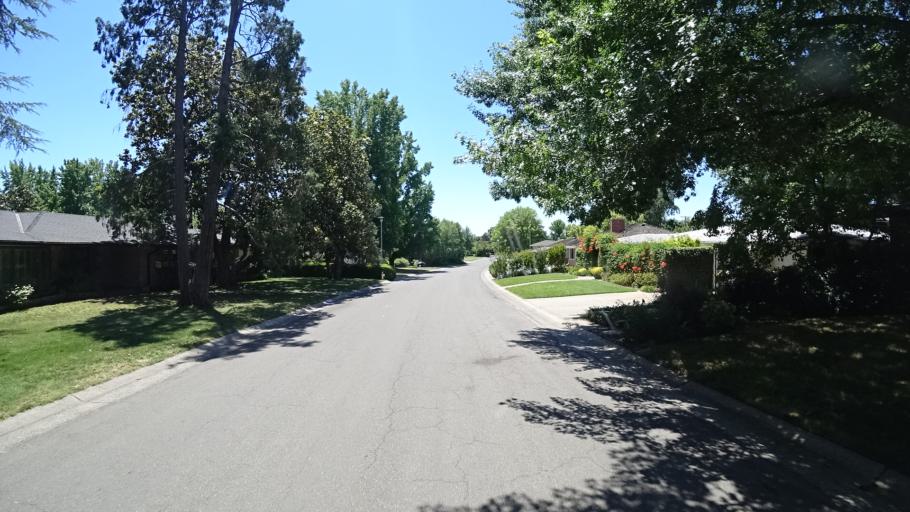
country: US
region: California
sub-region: Sacramento County
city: Sacramento
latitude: 38.5309
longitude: -121.5066
